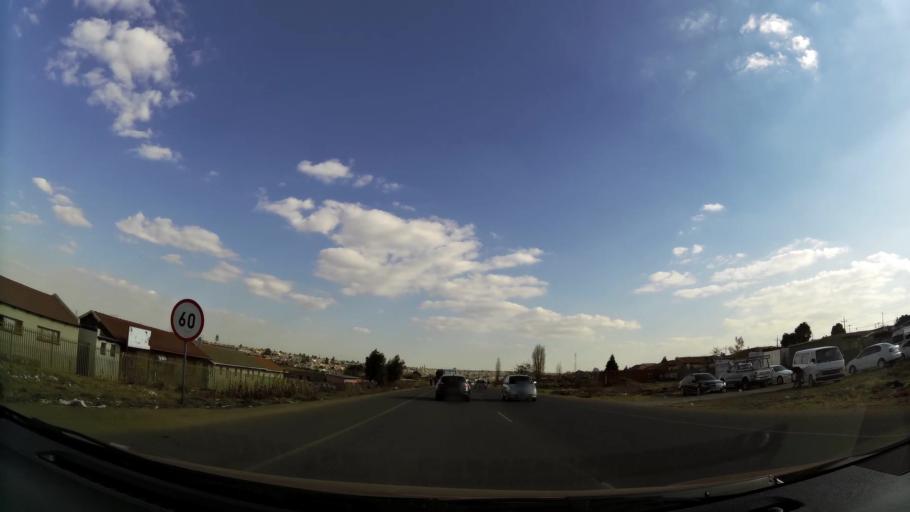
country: ZA
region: Gauteng
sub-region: Ekurhuleni Metropolitan Municipality
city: Tembisa
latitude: -25.9984
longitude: 28.1854
